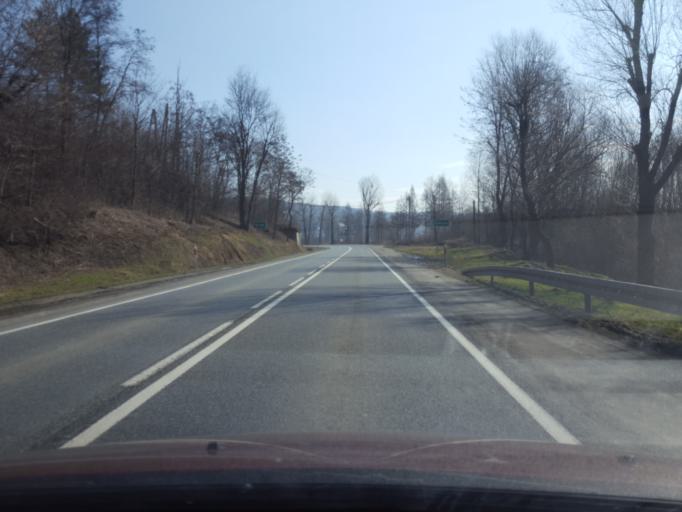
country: PL
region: Lesser Poland Voivodeship
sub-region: Powiat nowosadecki
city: Chelmiec
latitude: 49.6754
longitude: 20.6636
